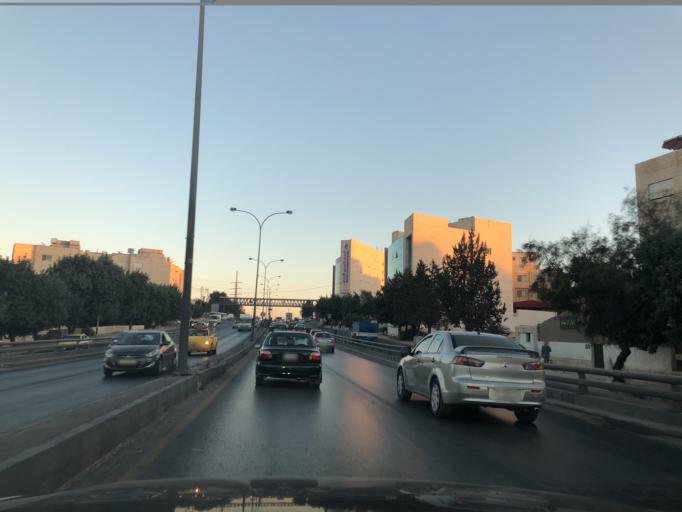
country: JO
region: Amman
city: Wadi as Sir
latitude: 31.9553
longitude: 35.8479
